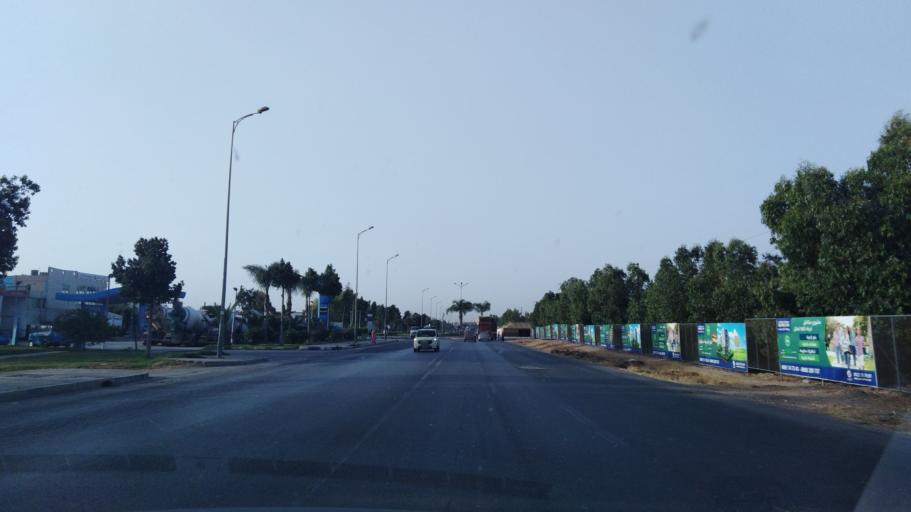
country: MA
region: Chaouia-Ouardigha
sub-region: Settat Province
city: Berrechid
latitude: 33.2510
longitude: -7.5845
